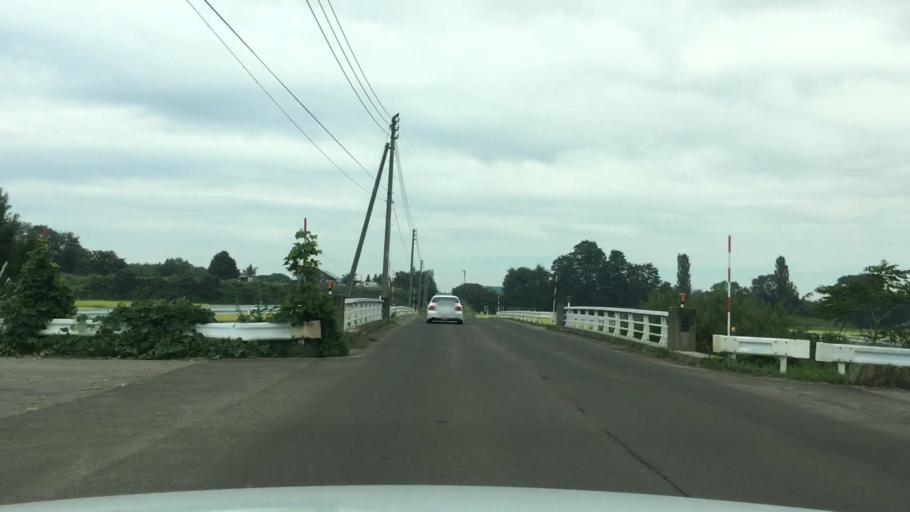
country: JP
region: Aomori
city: Hirosaki
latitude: 40.6503
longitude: 140.4224
